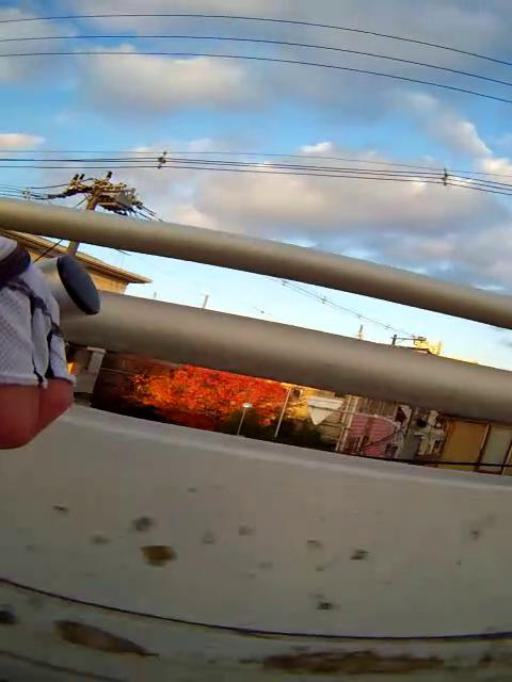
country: JP
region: Osaka
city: Osaka-shi
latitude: 34.7238
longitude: 135.4719
